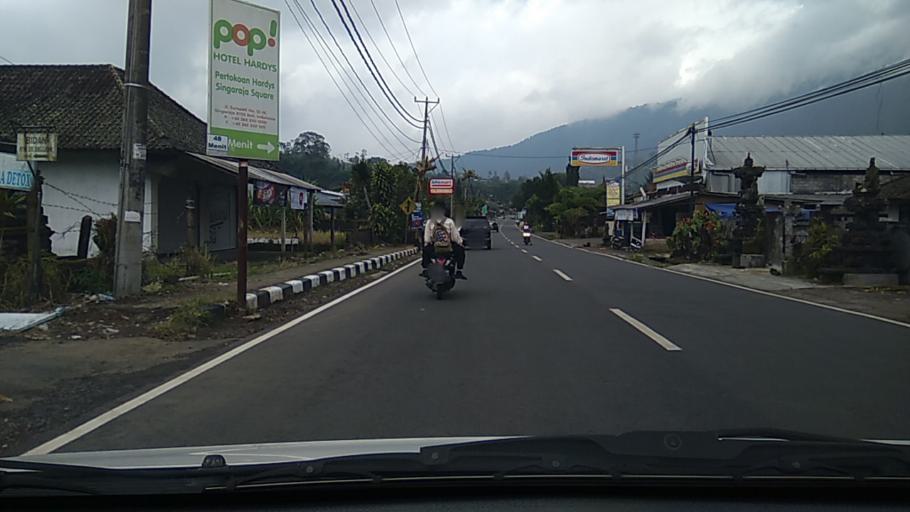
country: ID
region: Bali
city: Munduk
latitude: -8.2728
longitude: 115.1636
